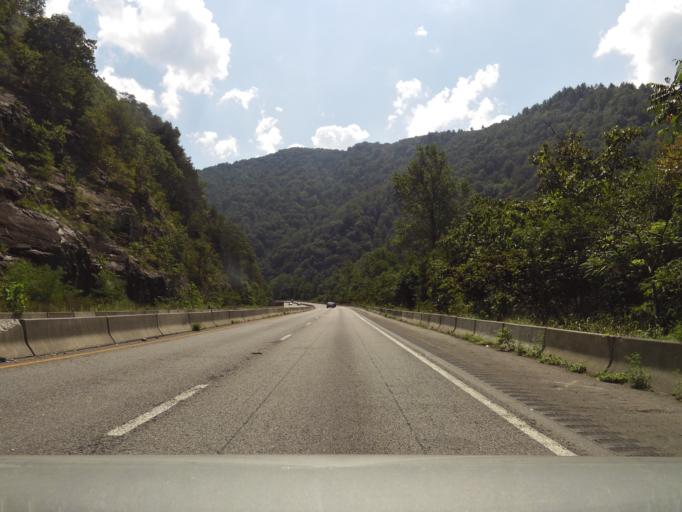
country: US
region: North Carolina
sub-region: Haywood County
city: Cove Creek
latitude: 35.7534
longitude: -83.0677
